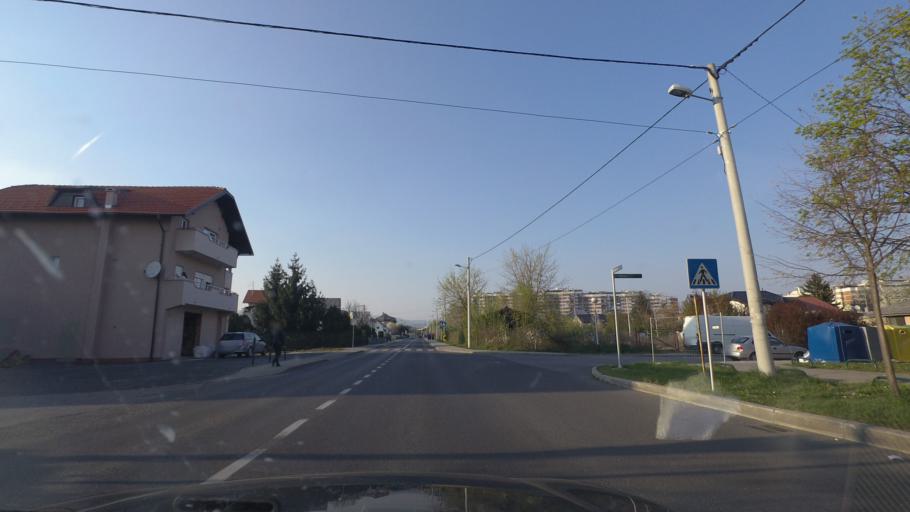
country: HR
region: Grad Zagreb
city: Dubrava
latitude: 45.8252
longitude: 16.0636
